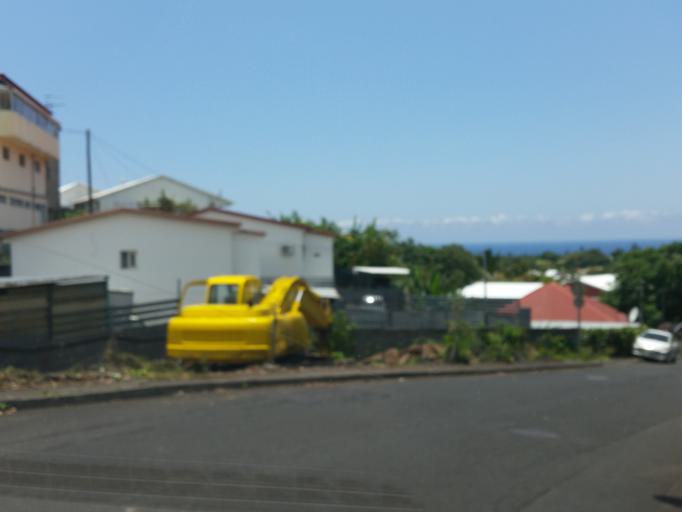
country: RE
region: Reunion
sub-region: Reunion
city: Sainte-Marie
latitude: -20.9158
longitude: 55.5064
